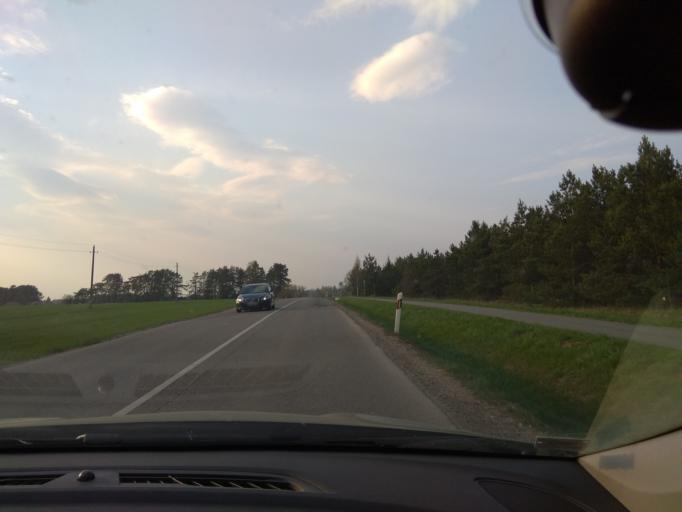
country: LT
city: Grigiskes
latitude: 54.6182
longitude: 25.1159
